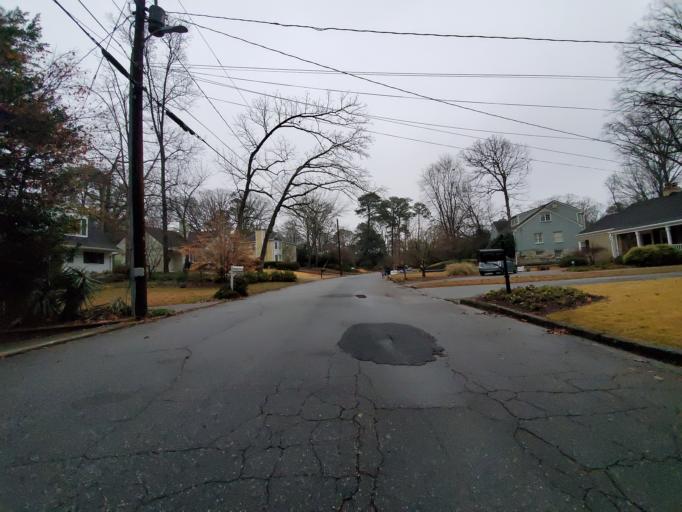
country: US
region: Georgia
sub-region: DeKalb County
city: North Decatur
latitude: 33.7940
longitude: -84.3094
